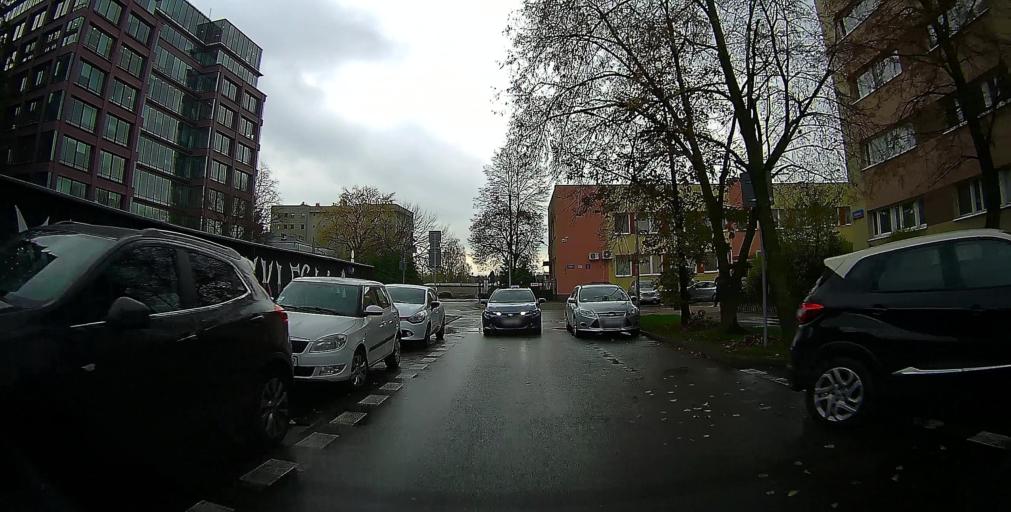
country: PL
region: Masovian Voivodeship
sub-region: Warszawa
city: Ochota
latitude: 52.1957
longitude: 20.9799
